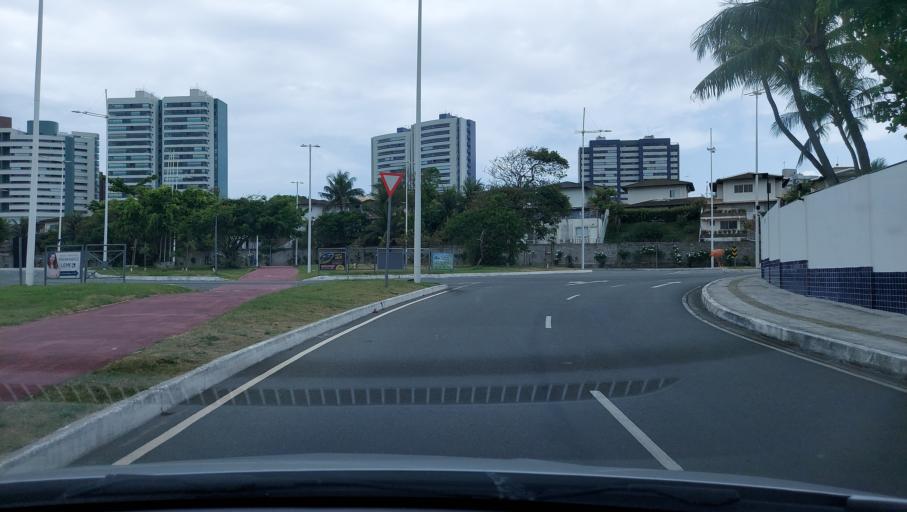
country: BR
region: Bahia
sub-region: Lauro De Freitas
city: Lauro de Freitas
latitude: -12.9573
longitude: -38.4010
